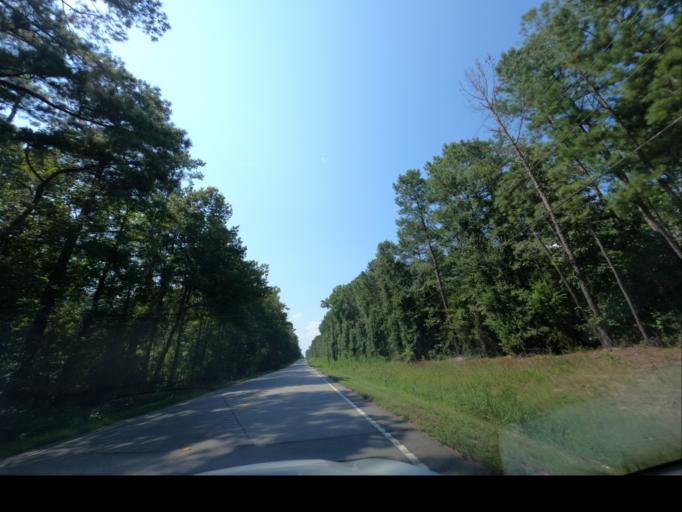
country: US
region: South Carolina
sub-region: Richland County
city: Hopkins
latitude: 33.9120
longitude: -80.9408
